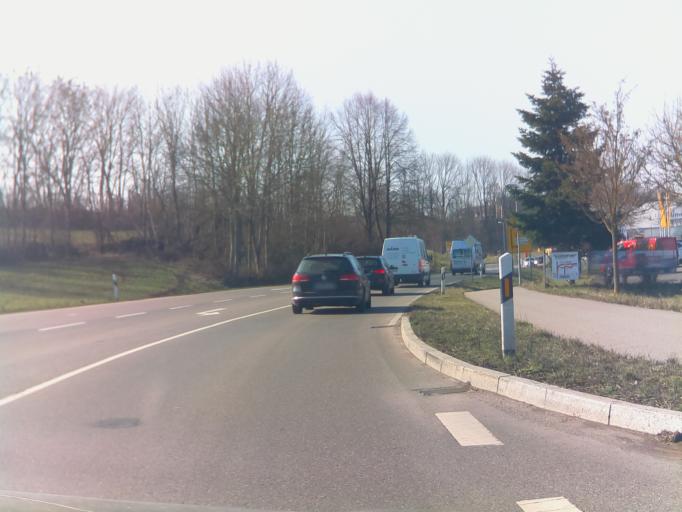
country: DE
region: Baden-Wuerttemberg
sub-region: Karlsruhe Region
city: Horb am Neckar
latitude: 48.4575
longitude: 8.7022
